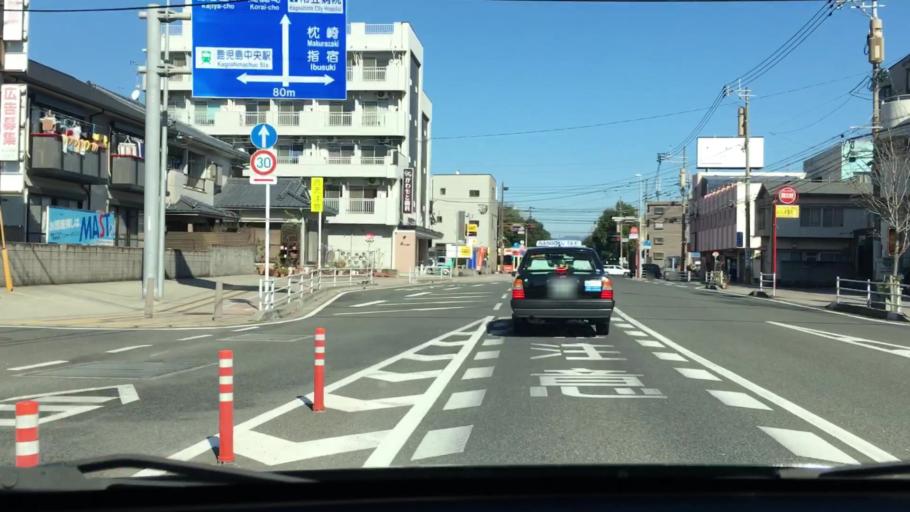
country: JP
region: Kagoshima
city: Kagoshima-shi
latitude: 31.5639
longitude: 130.5450
